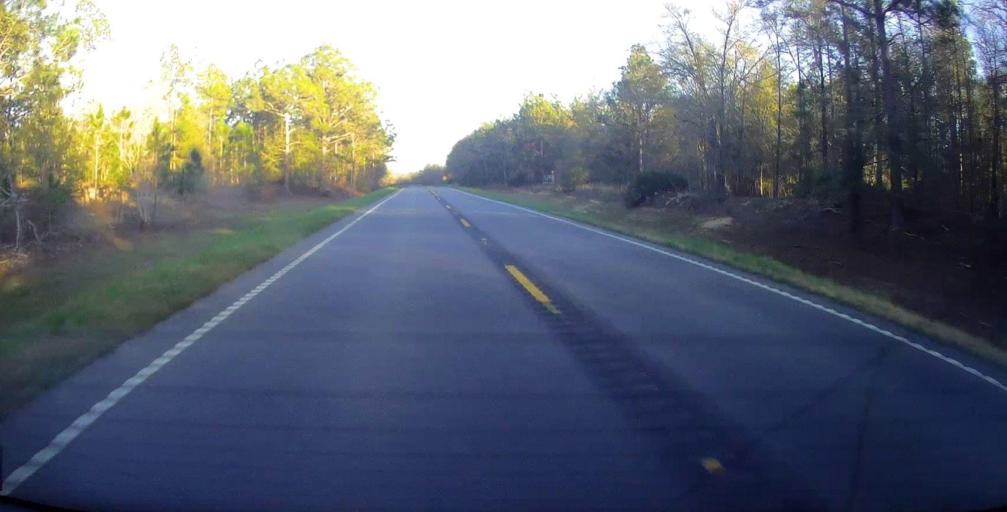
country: US
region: Georgia
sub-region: Wilcox County
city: Rochelle
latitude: 31.9461
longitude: -83.5580
